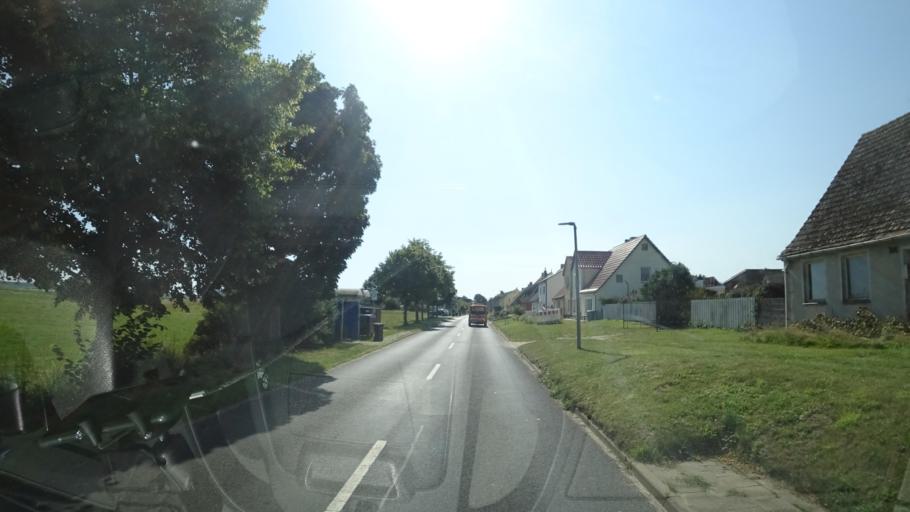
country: DE
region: Mecklenburg-Vorpommern
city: Kroslin
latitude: 54.1223
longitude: 13.7471
